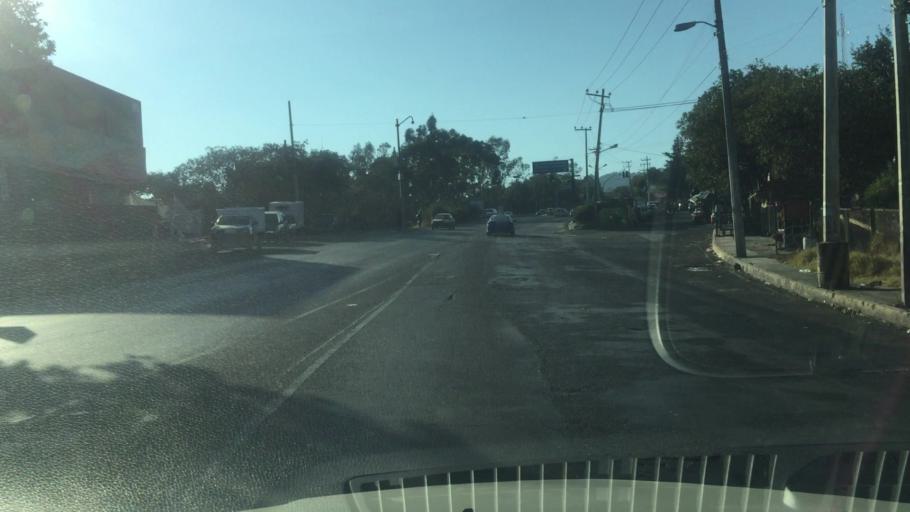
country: MX
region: Mexico City
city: Tlalpan
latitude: 19.2727
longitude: -99.2062
